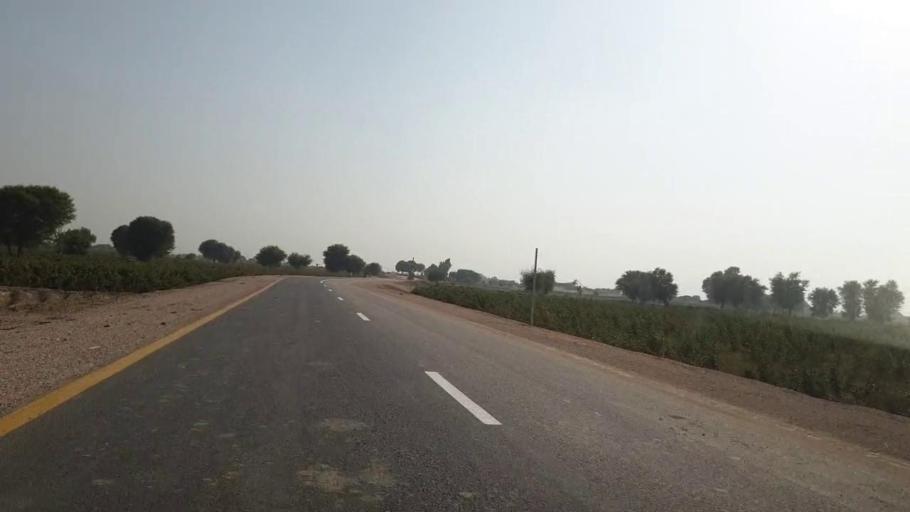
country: PK
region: Sindh
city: Bhan
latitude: 26.5054
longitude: 67.7831
